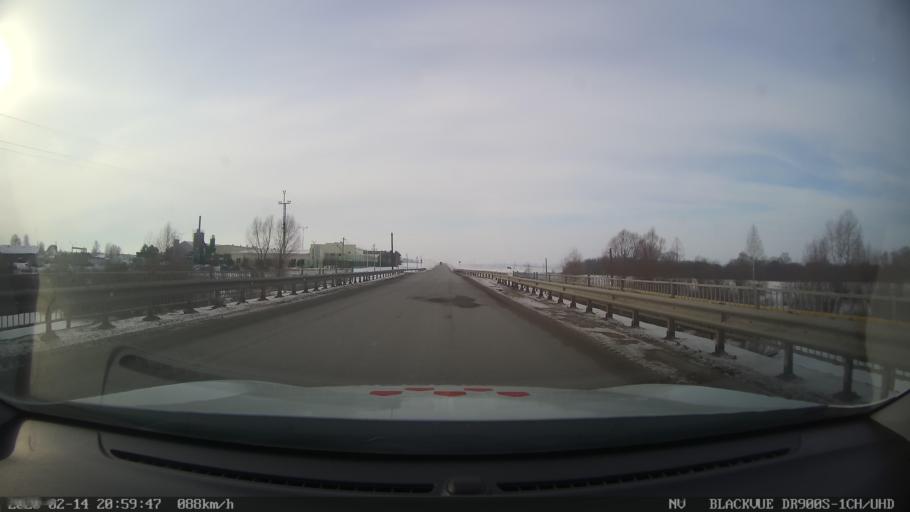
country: RU
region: Tatarstan
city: Kuybyshevskiy Zaton
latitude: 55.1758
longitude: 49.2334
